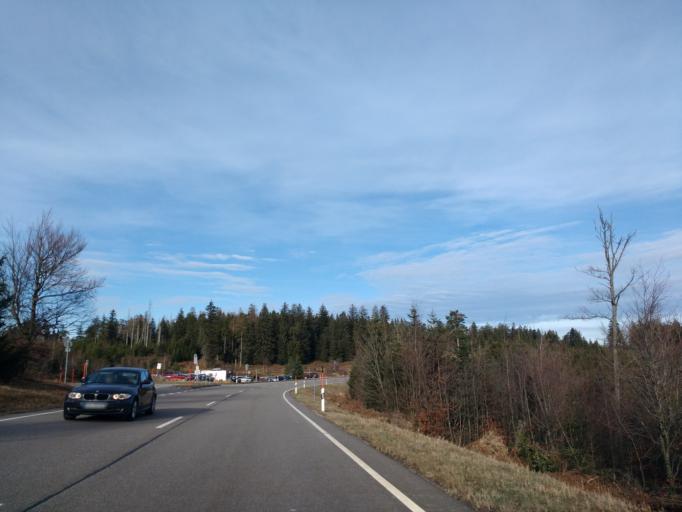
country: DE
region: Baden-Wuerttemberg
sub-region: Freiburg Region
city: Oppenau
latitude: 48.5057
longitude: 8.2241
